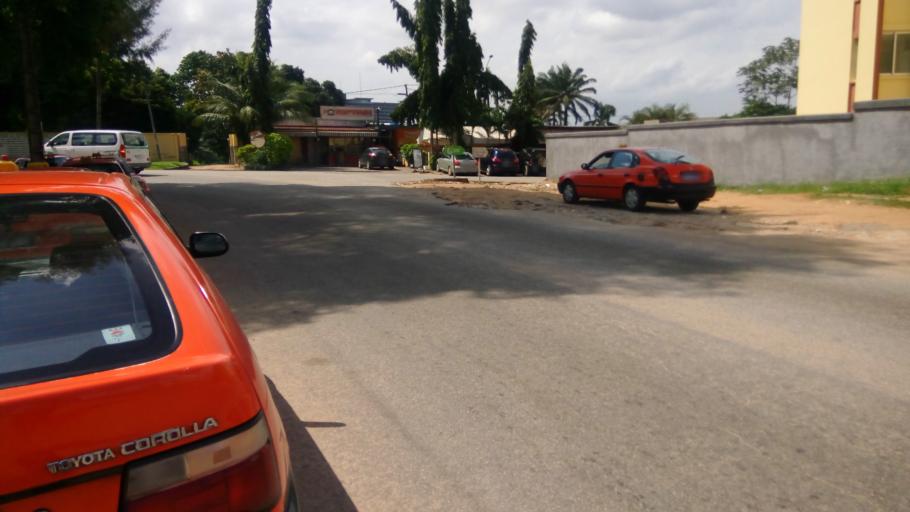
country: CI
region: Lagunes
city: Abidjan
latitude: 5.3386
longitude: -3.9962
